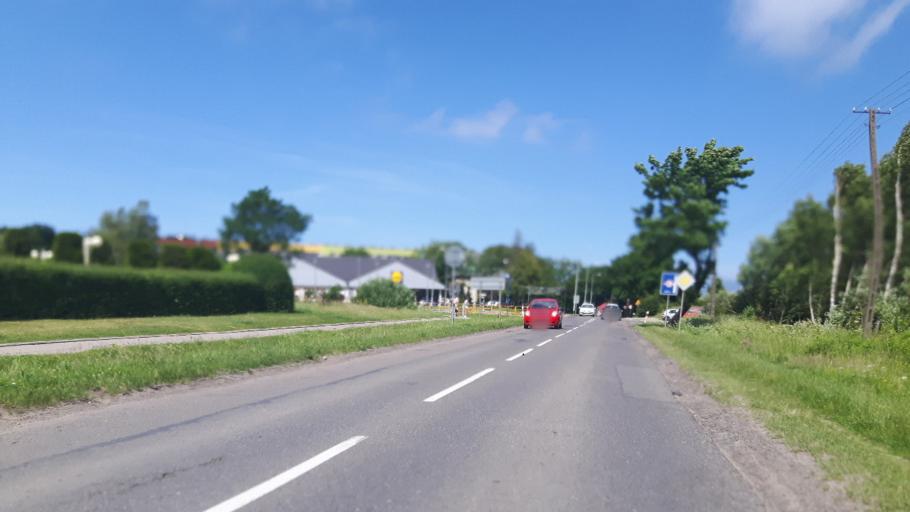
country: PL
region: Pomeranian Voivodeship
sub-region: Powiat slupski
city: Ustka
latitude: 54.5744
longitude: 16.8525
